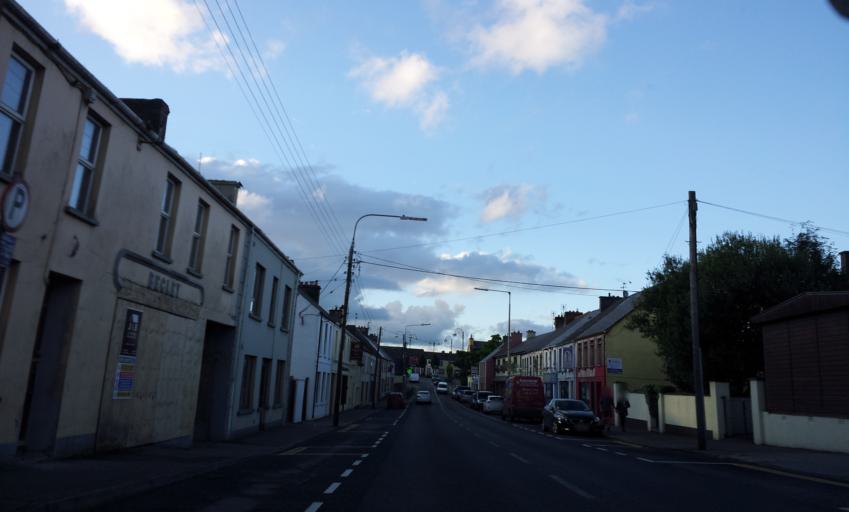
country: IE
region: Munster
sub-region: County Limerick
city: Abbeyfeale
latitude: 52.3826
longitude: -9.3015
